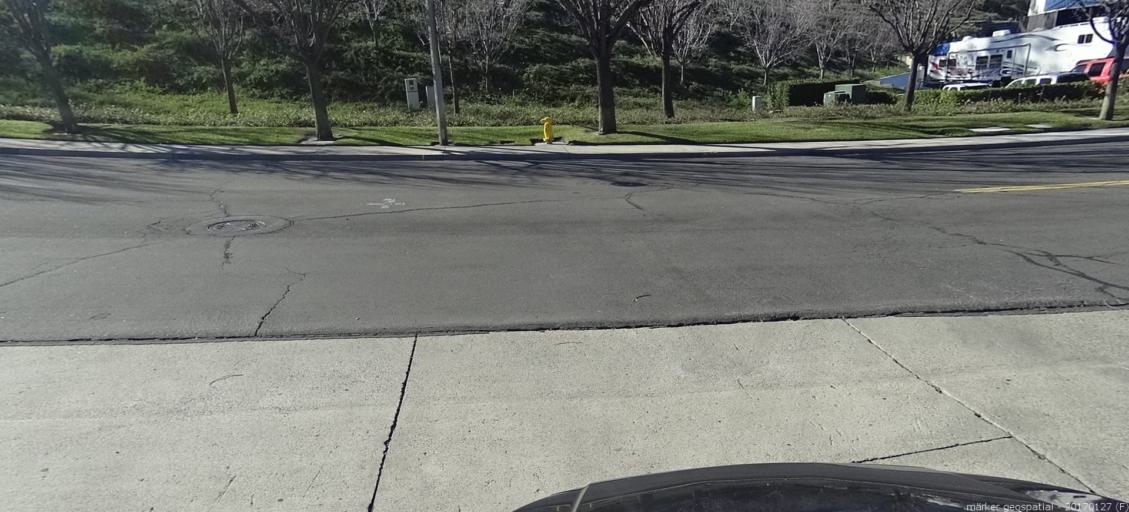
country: US
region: California
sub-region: Orange County
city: Foothill Ranch
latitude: 33.6635
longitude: -117.6649
